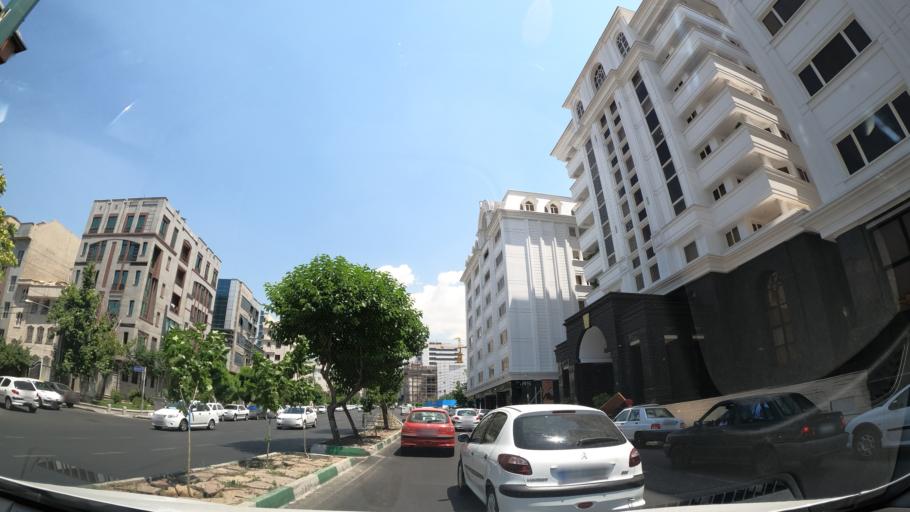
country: IR
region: Tehran
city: Tajrish
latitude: 35.7677
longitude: 51.3788
